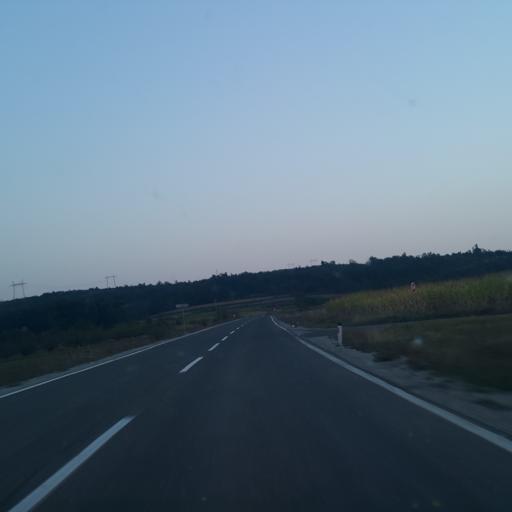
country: RS
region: Central Serbia
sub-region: Nisavski Okrug
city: Svrljig
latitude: 43.4466
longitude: 22.1713
